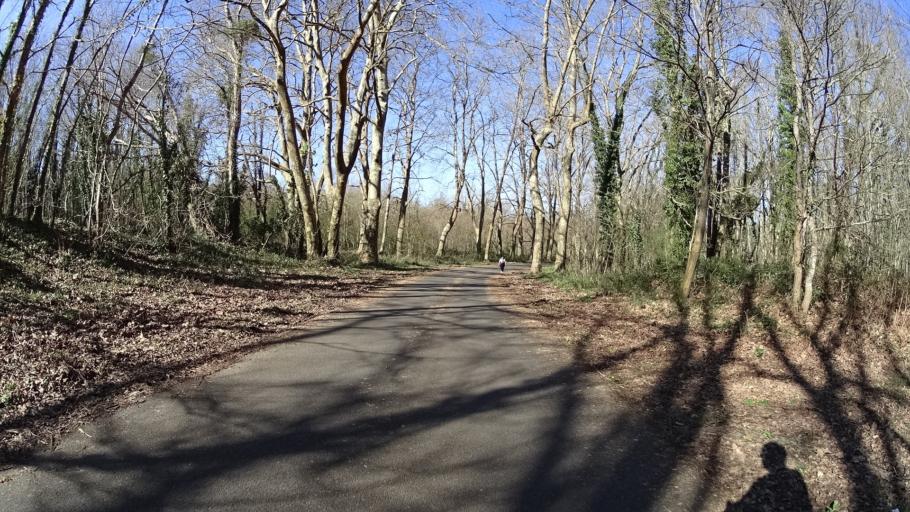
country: FR
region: Aquitaine
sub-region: Departement des Landes
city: Mees
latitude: 43.7462
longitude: -1.0968
